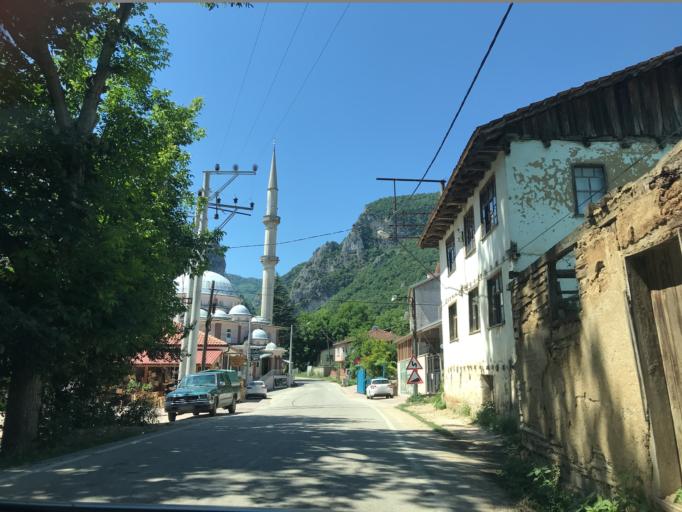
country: TR
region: Bursa
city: Tahtakopru
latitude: 39.9513
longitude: 29.5960
